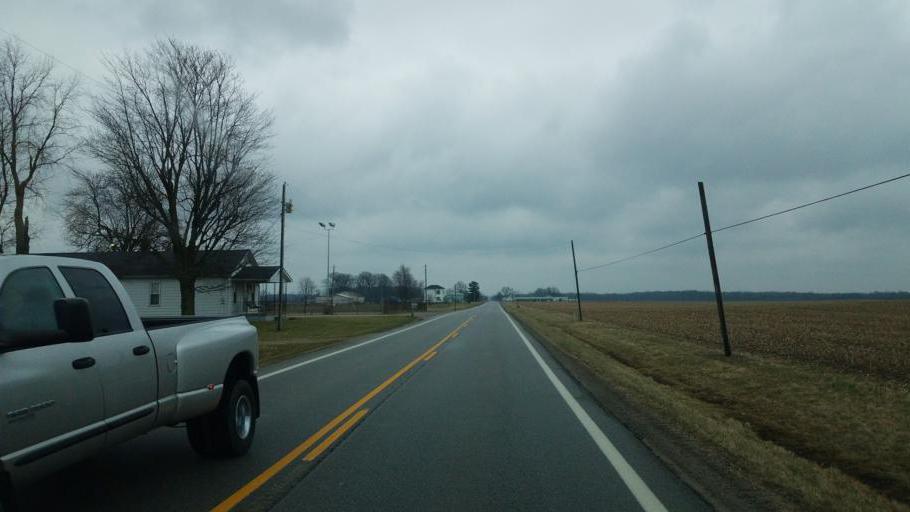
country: US
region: Ohio
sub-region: Delaware County
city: Ashley
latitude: 40.4081
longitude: -82.9324
